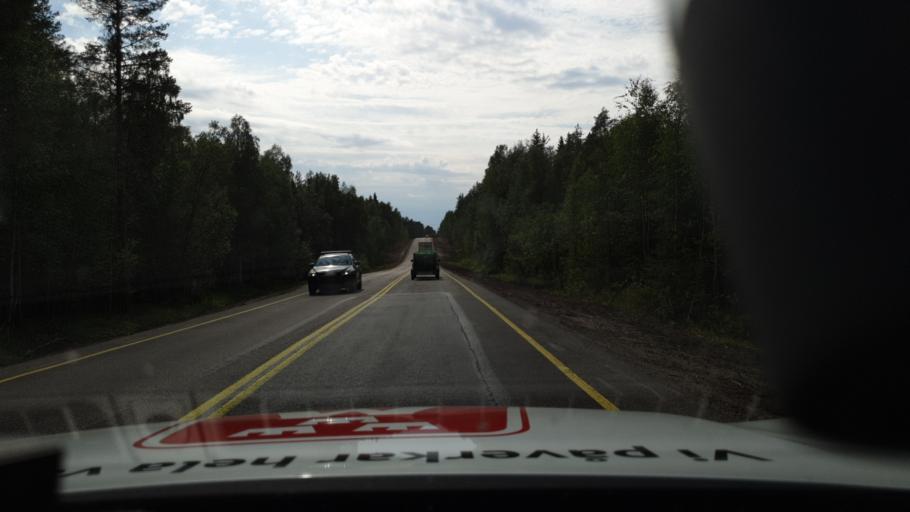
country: SE
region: Norrbotten
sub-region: Lulea Kommun
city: Ranea
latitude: 65.8666
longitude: 22.3196
